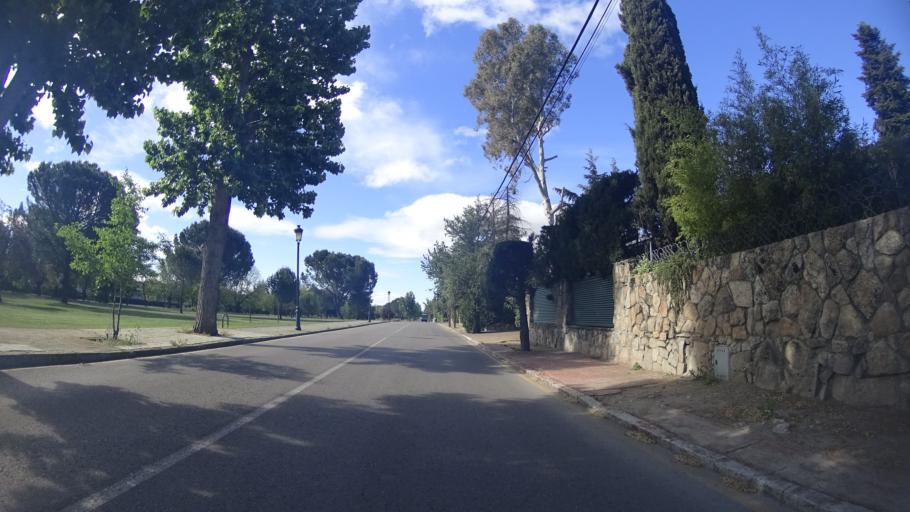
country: ES
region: Madrid
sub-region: Provincia de Madrid
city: Villanueva del Pardillo
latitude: 40.4764
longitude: -3.9420
